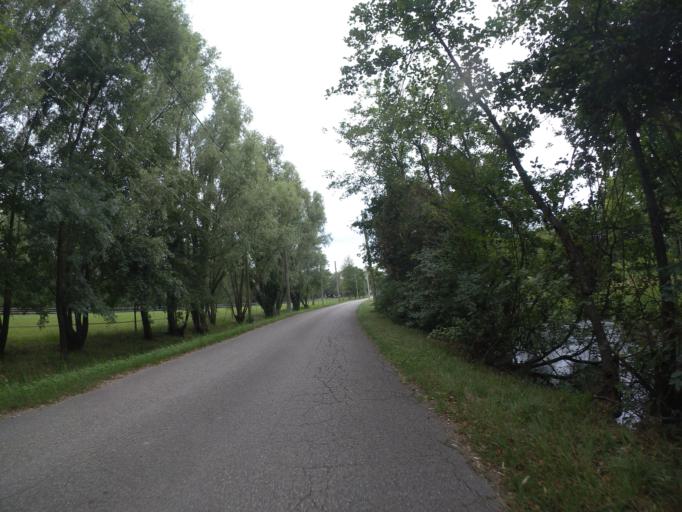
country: IT
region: Friuli Venezia Giulia
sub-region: Provincia di Udine
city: Rivignano
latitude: 45.8874
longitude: 13.0669
